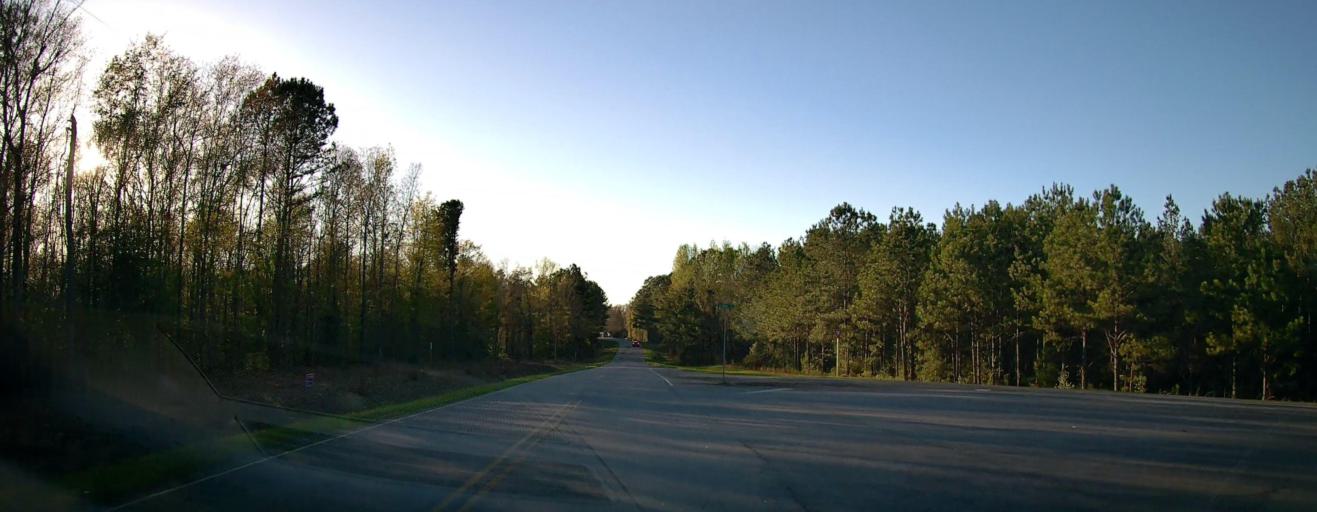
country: US
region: Georgia
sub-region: Wilkinson County
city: Gordon
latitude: 32.8744
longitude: -83.2484
